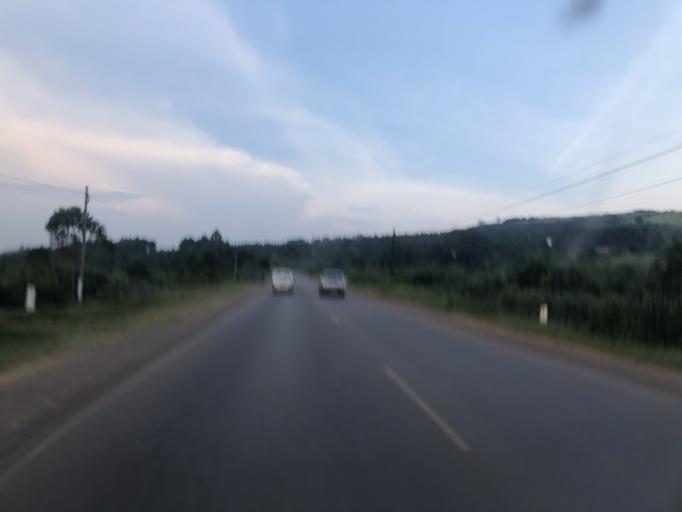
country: UG
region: Central Region
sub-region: Mpigi District
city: Mpigi
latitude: 0.2268
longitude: 32.3421
